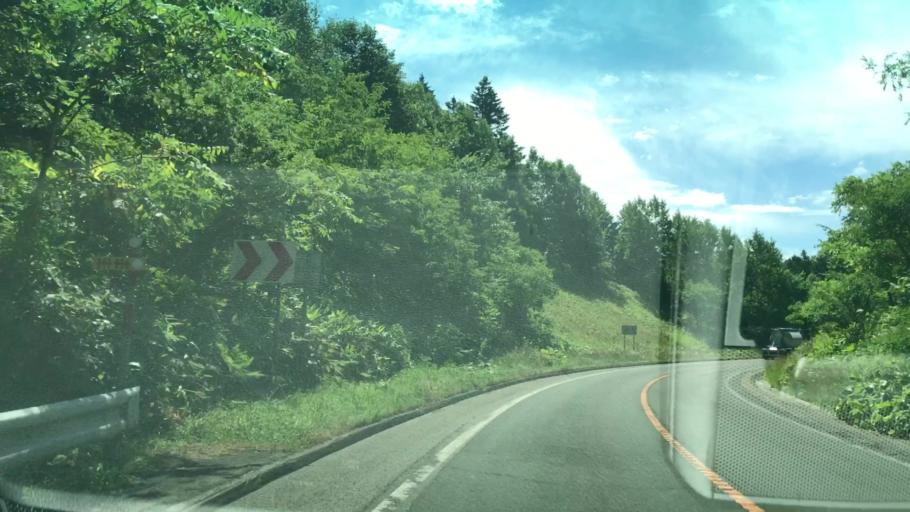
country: JP
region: Hokkaido
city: Shimo-furano
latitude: 42.9200
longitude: 142.4473
